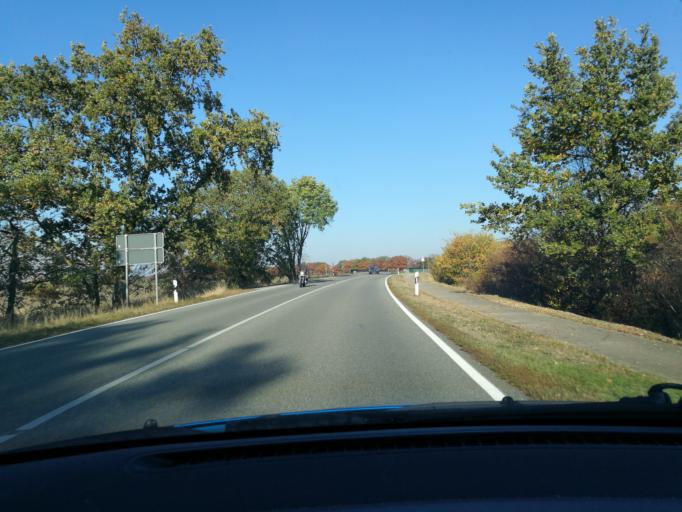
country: DE
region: Mecklenburg-Vorpommern
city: Domitz
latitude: 53.1547
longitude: 11.2381
